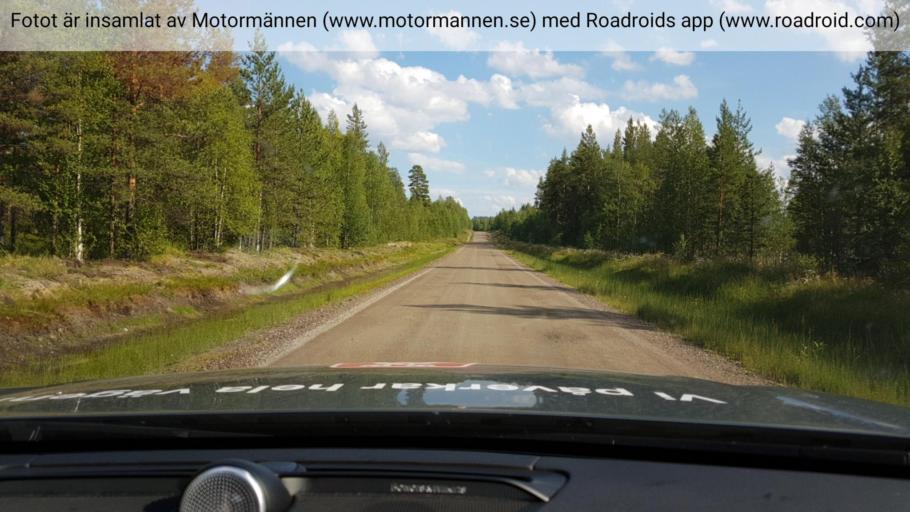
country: SE
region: Jaemtland
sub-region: Stroemsunds Kommun
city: Stroemsund
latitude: 64.0133
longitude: 15.9461
